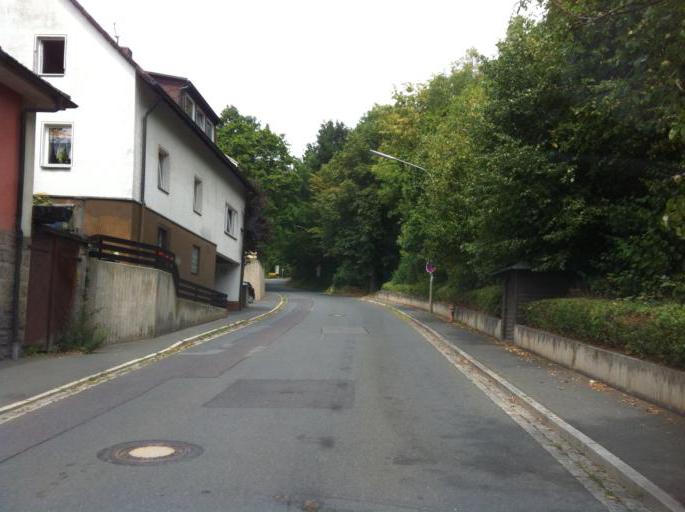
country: DE
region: Bavaria
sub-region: Upper Franconia
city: Goldkronach
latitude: 50.0091
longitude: 11.6858
